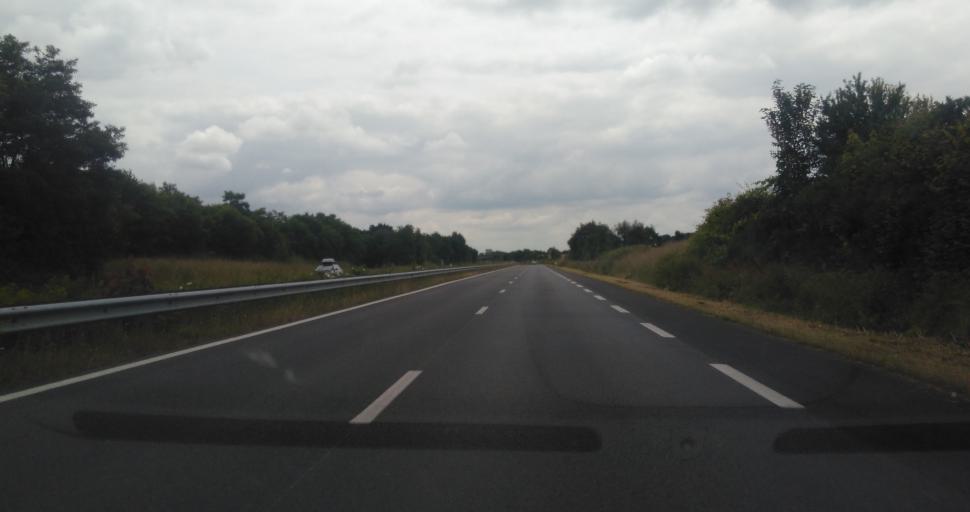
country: FR
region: Pays de la Loire
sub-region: Departement de la Vendee
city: Bournezeau
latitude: 46.6350
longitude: -1.1828
